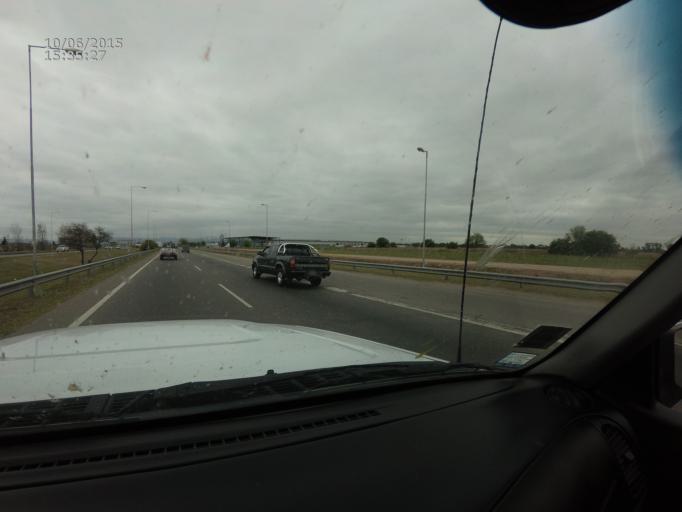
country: AR
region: Cordoba
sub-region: Departamento de Capital
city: Cordoba
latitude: -31.3540
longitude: -64.1916
